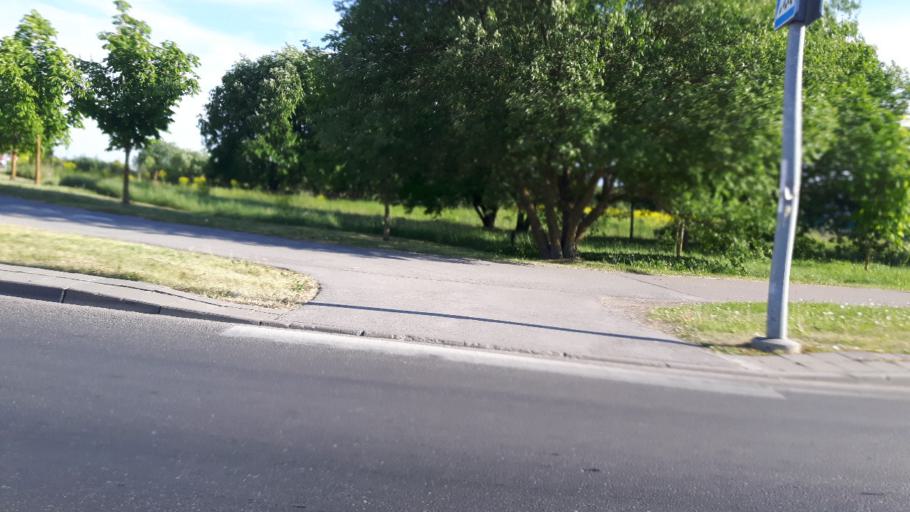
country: EE
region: Harju
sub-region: Tallinna linn
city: Kose
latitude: 59.4514
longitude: 24.8590
